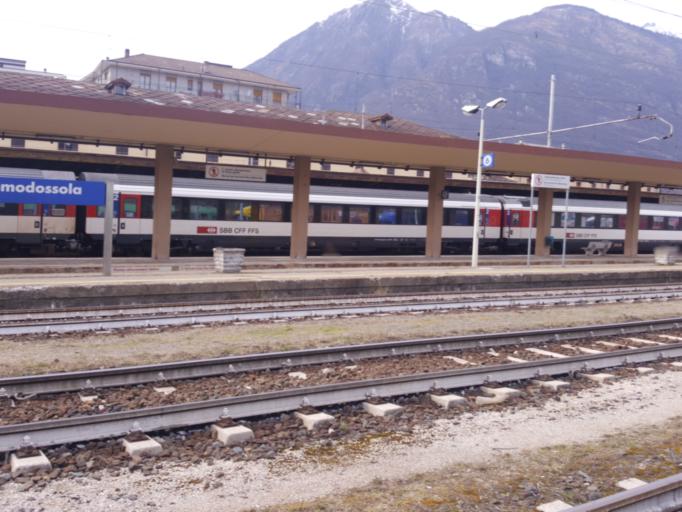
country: IT
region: Piedmont
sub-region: Provincia Verbano-Cusio-Ossola
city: Domodossola
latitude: 46.1160
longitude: 8.2974
